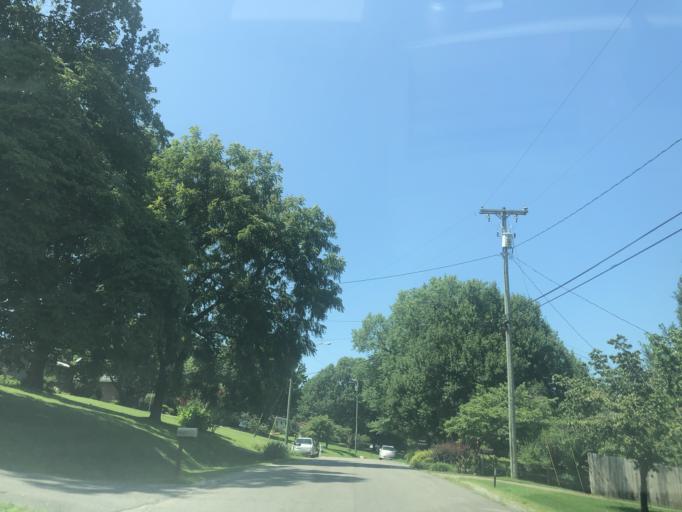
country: US
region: Tennessee
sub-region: Davidson County
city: Nashville
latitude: 36.1797
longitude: -86.7148
